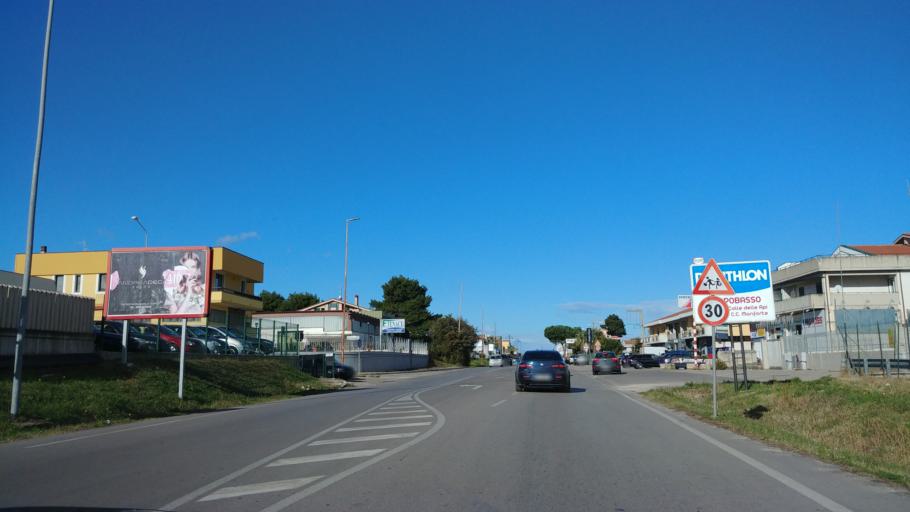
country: IT
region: Molise
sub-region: Provincia di Campobasso
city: Termoli
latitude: 41.9841
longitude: 15.0048
